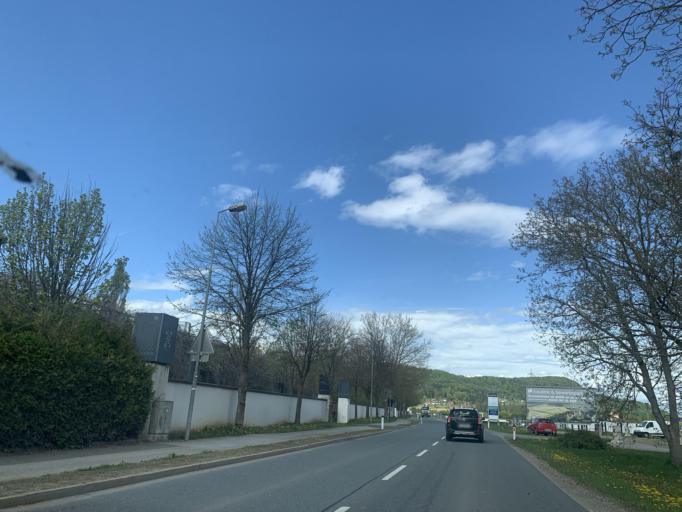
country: AT
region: Styria
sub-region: Politischer Bezirk Leibnitz
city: Lang
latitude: 46.8409
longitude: 15.5180
